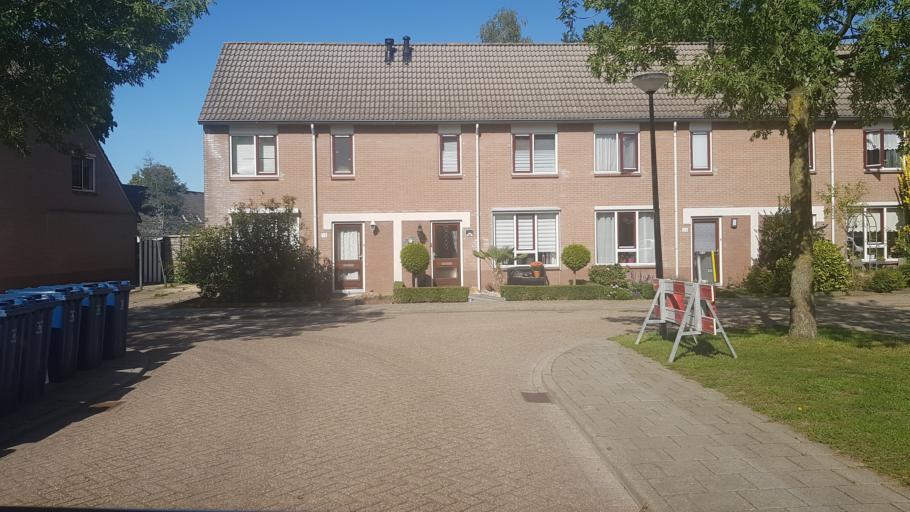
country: NL
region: Gelderland
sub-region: Gemeente Apeldoorn
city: Beekbergen
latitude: 52.1642
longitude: 5.9669
